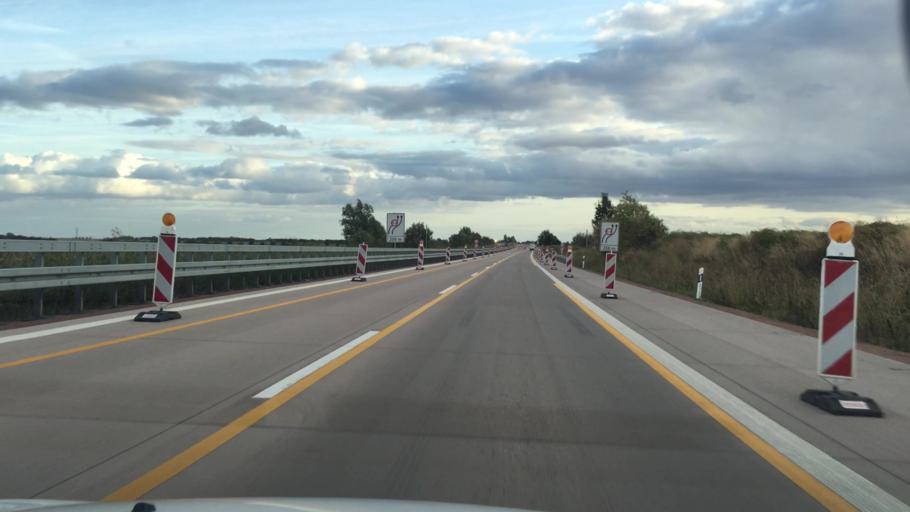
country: DE
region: Saxony-Anhalt
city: Nauendorf
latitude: 51.6104
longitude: 11.8702
